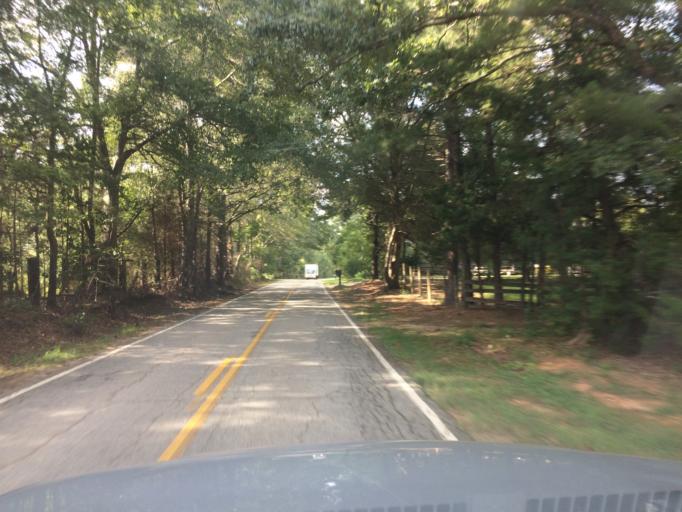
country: US
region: South Carolina
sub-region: Spartanburg County
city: Woodruff
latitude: 34.7785
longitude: -82.1126
